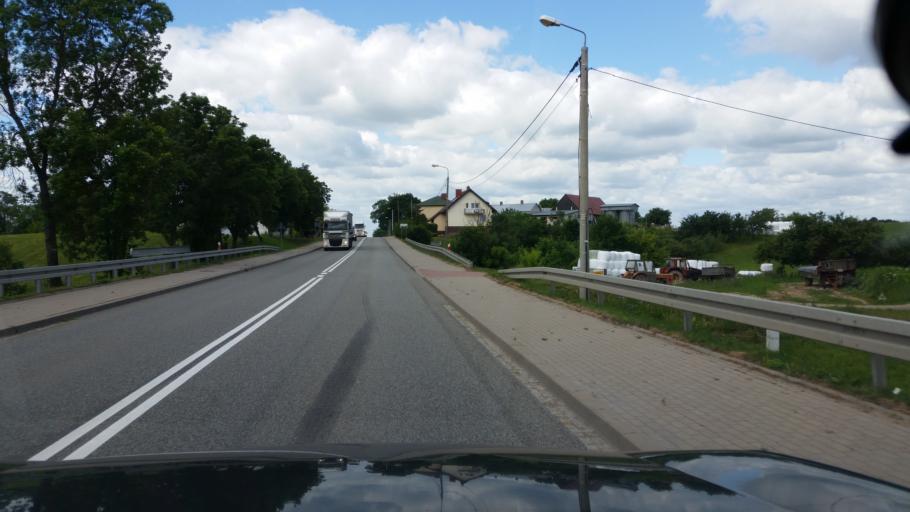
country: PL
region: Podlasie
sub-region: Powiat grajewski
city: Rajgrod
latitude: 53.7318
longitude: 22.7130
